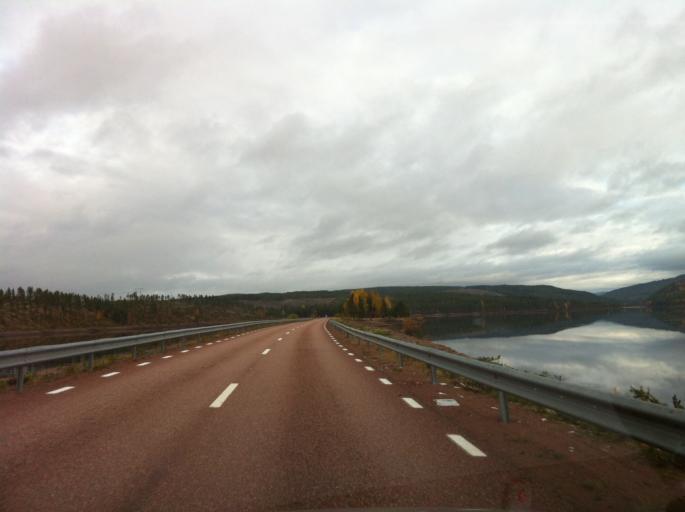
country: SE
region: Dalarna
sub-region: Alvdalens Kommun
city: AElvdalen
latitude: 61.2973
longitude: 13.7307
